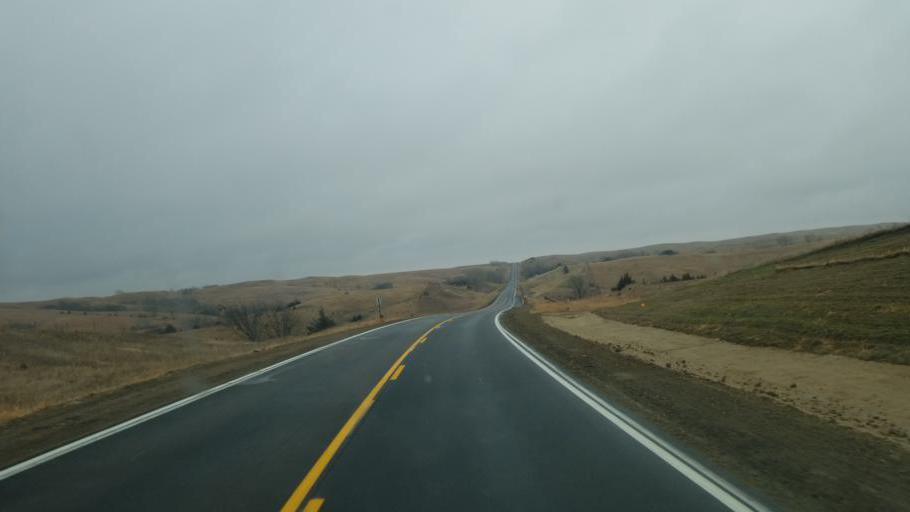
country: US
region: Nebraska
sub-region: Knox County
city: Center
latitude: 42.5968
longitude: -97.8553
